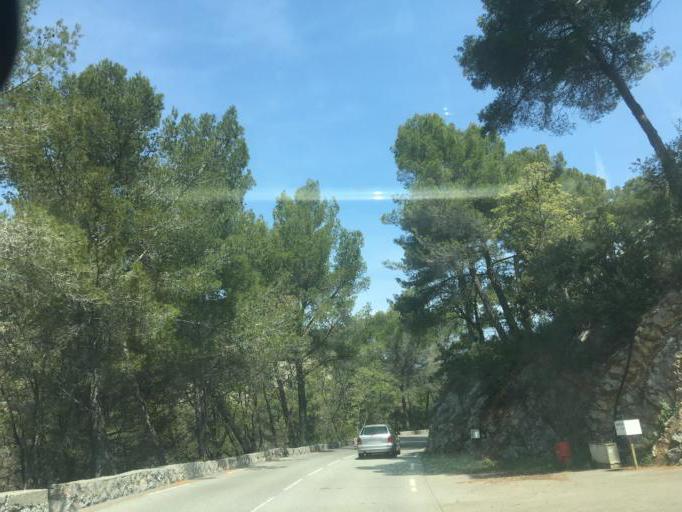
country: FR
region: Provence-Alpes-Cote d'Azur
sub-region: Departement des Alpes-Maritimes
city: Saint-Martin-du-Var
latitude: 43.8358
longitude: 7.2092
